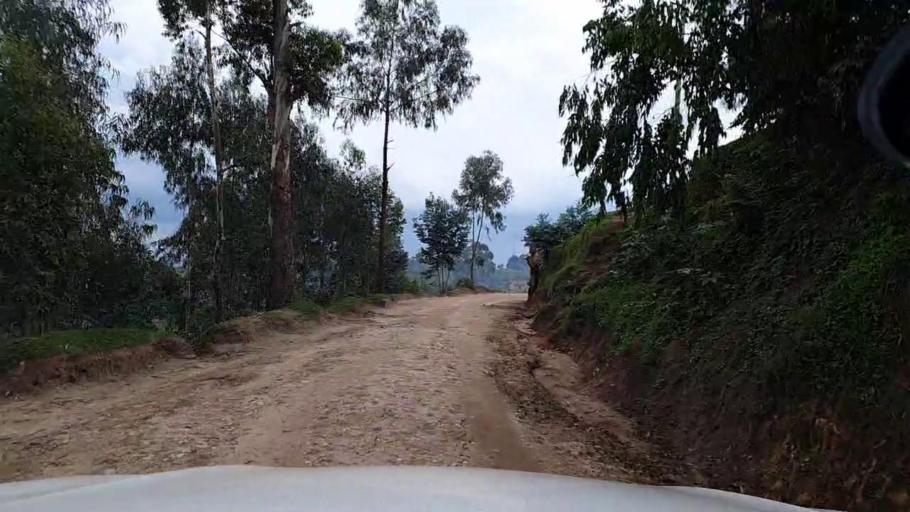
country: BI
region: Kayanza
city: Kayanza
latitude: -2.7984
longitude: 29.4970
